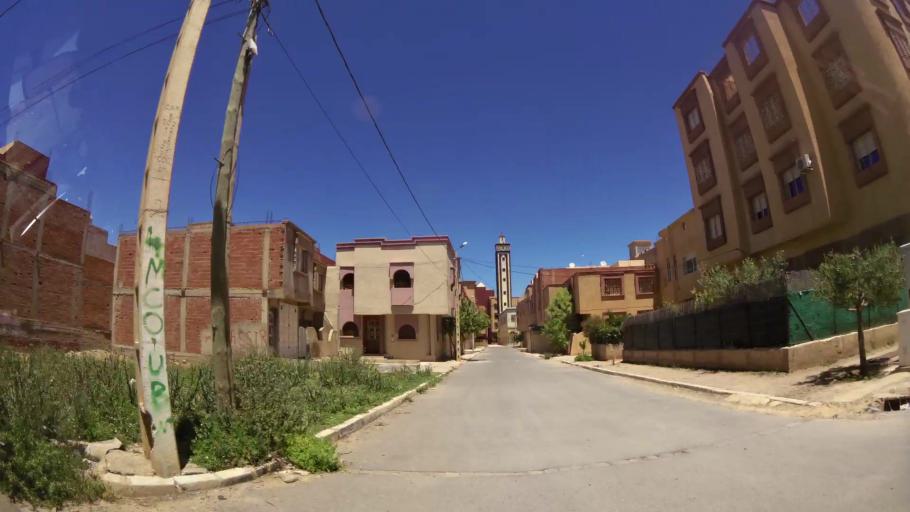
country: MA
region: Oriental
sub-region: Oujda-Angad
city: Oujda
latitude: 34.6744
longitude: -1.8774
